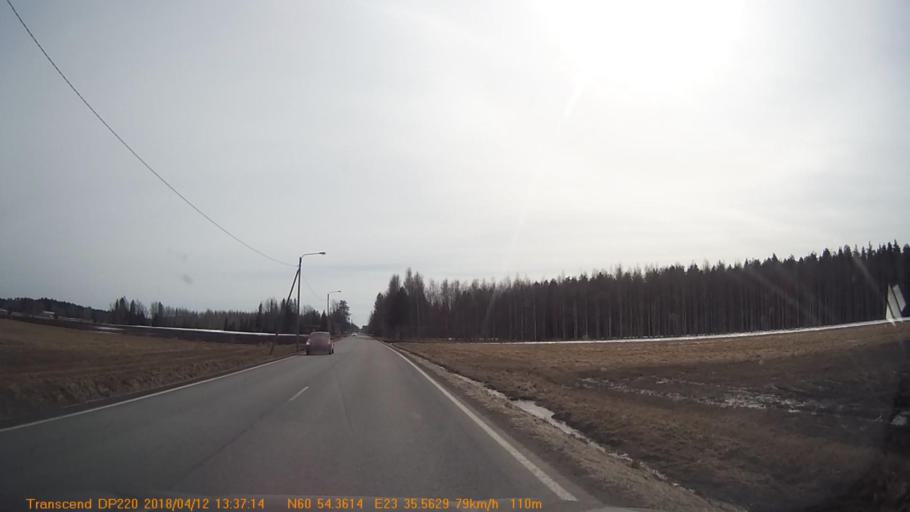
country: FI
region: Haeme
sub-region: Forssa
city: Forssa
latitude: 60.9056
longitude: 23.5928
